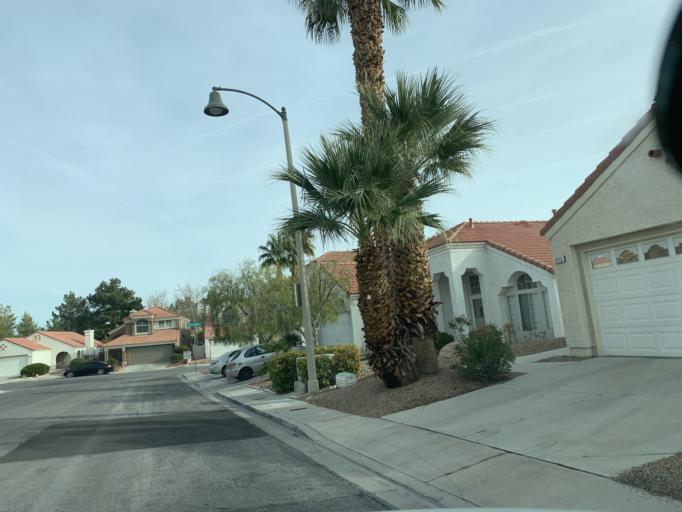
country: US
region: Nevada
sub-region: Clark County
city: Summerlin South
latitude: 36.1346
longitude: -115.3077
